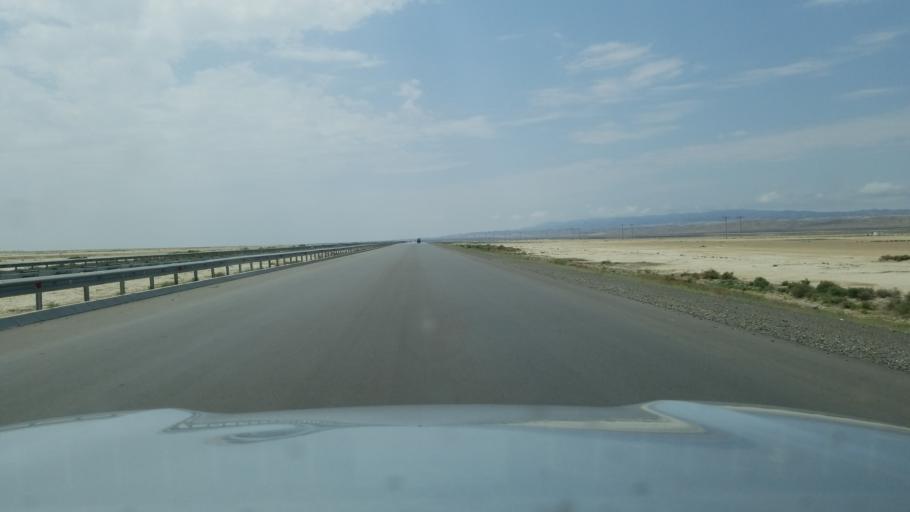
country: TM
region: Balkan
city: Gazanjyk
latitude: 39.2804
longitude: 55.2112
